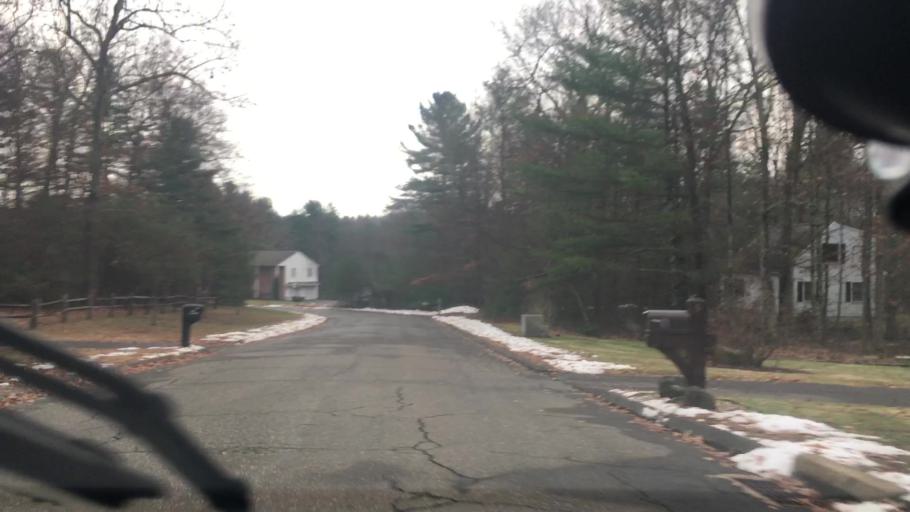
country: US
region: Connecticut
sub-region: Tolland County
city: Stafford Springs
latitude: 41.9821
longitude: -72.3253
